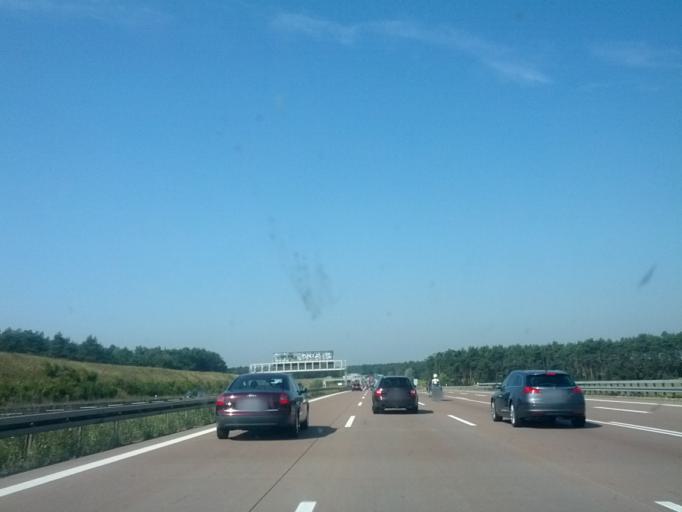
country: DE
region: Brandenburg
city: Michendorf
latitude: 52.3009
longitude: 13.0624
